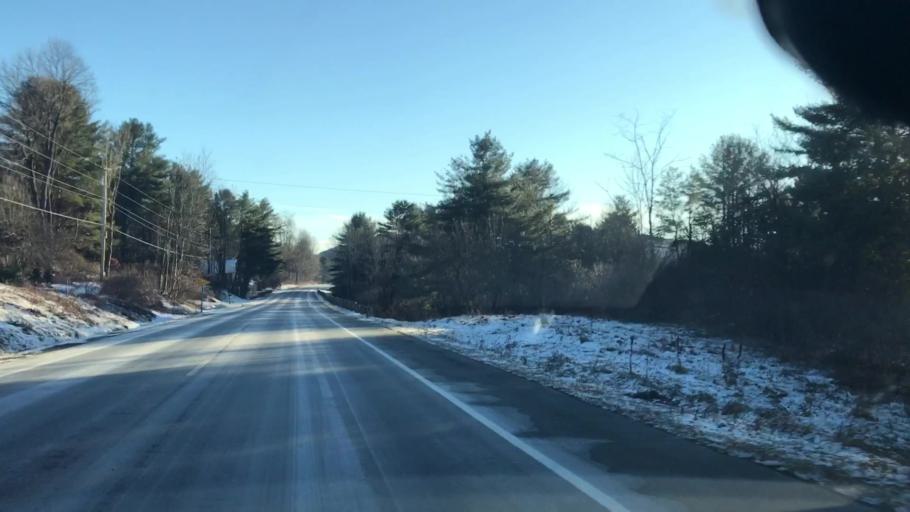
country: US
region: New Hampshire
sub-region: Grafton County
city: Lyme Town Offices
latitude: 43.8589
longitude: -72.1553
